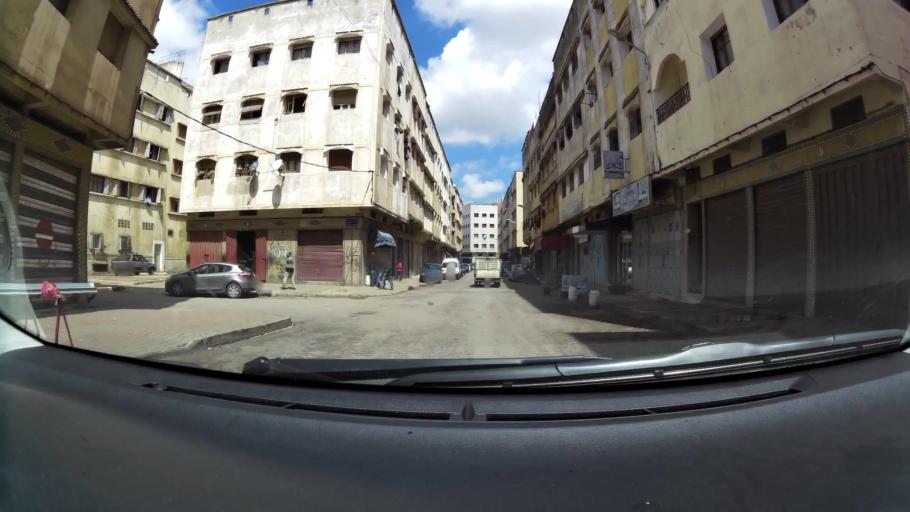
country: MA
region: Grand Casablanca
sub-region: Casablanca
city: Casablanca
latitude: 33.5387
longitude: -7.5675
